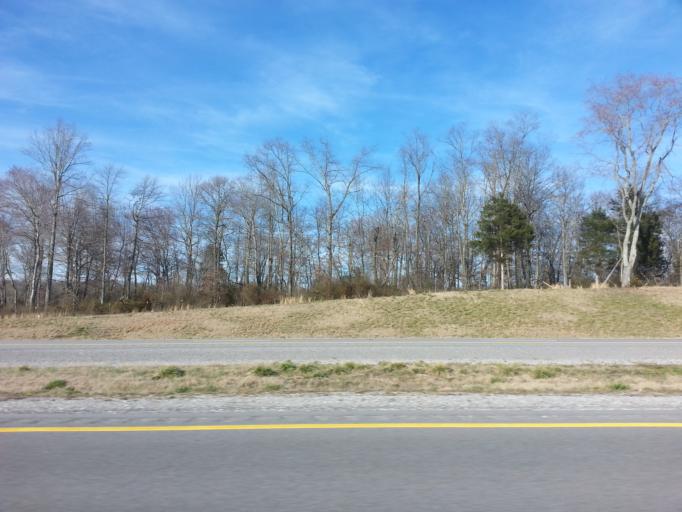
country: US
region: Tennessee
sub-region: Warren County
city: McMinnville
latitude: 35.7261
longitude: -85.8999
